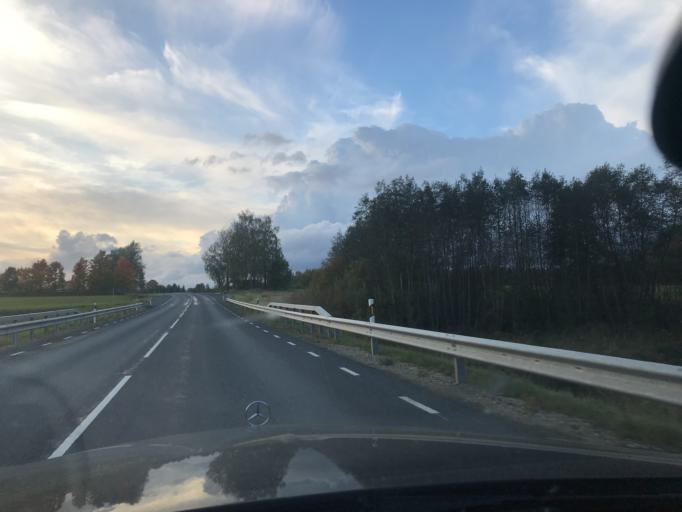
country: EE
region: Vorumaa
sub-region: Antsla vald
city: Vana-Antsla
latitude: 57.9109
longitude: 26.4110
